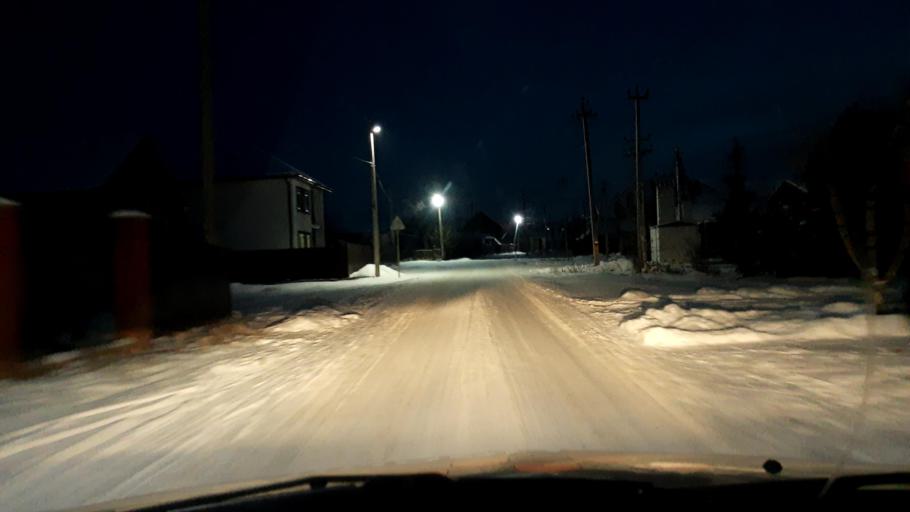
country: RU
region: Bashkortostan
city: Ufa
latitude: 54.6124
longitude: 55.9486
